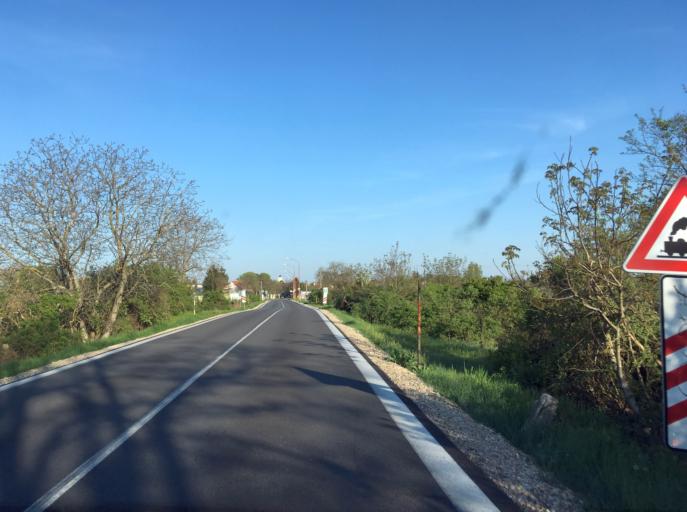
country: AT
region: Burgenland
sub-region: Politischer Bezirk Neusiedl am See
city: Deutsch Jahrndorf
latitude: 48.0589
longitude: 17.1351
